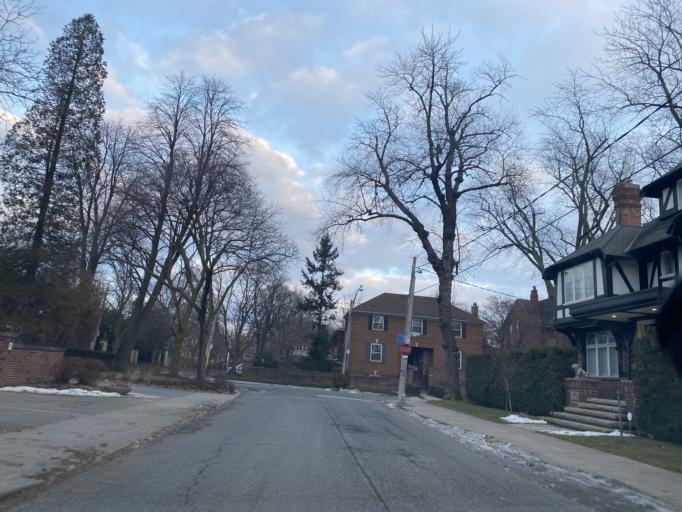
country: CA
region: Ontario
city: Toronto
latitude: 43.6766
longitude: -79.3728
